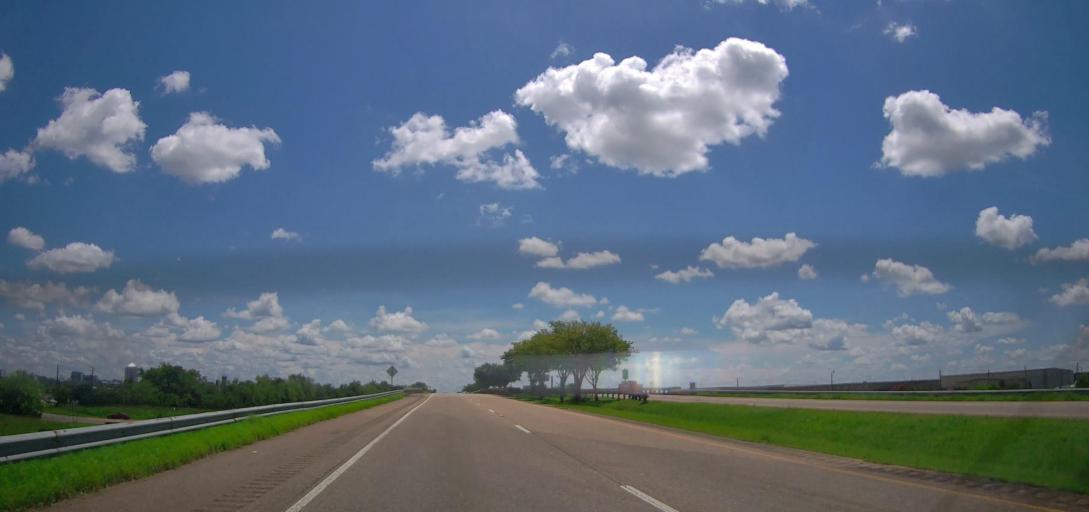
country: US
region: Alabama
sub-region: Montgomery County
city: Montgomery
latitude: 32.4043
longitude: -86.3087
